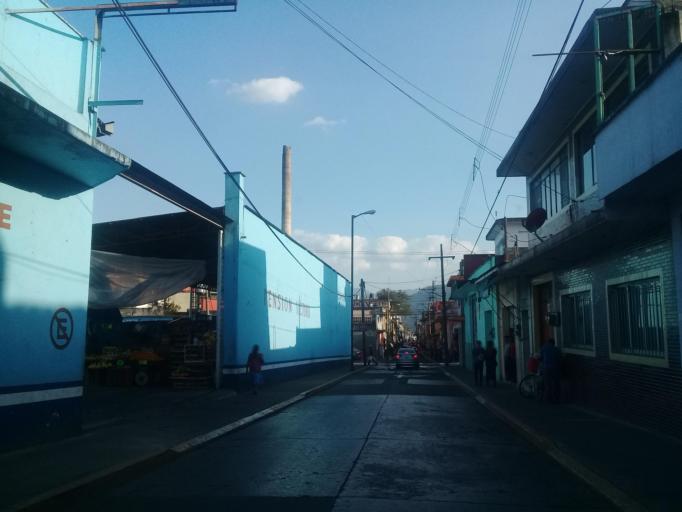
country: MX
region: Veracruz
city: Orizaba
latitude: 18.8521
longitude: -97.1077
